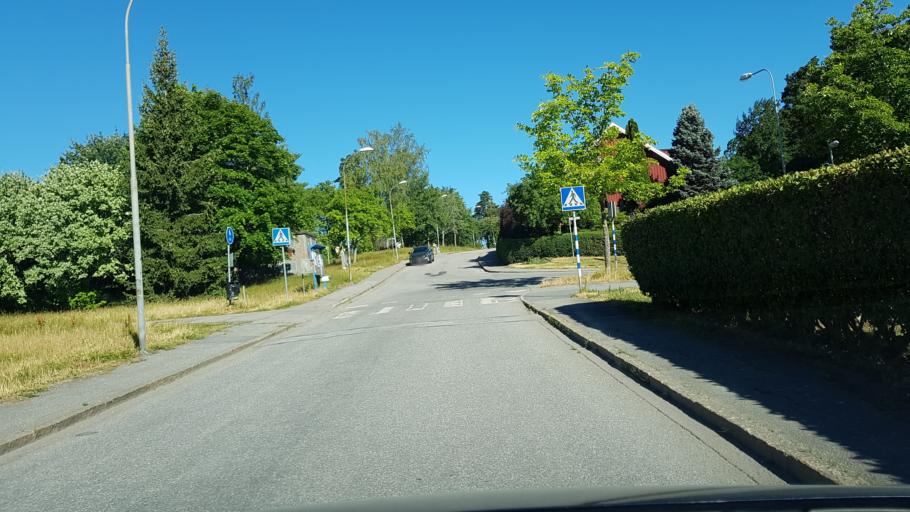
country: SE
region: Stockholm
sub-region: Jarfalla Kommun
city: Jakobsberg
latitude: 59.4142
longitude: 17.8204
